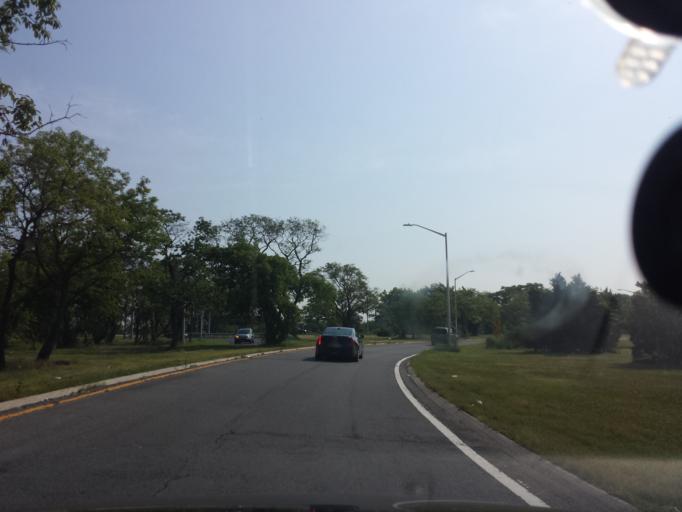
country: US
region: New York
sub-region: Kings County
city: Brooklyn
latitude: 40.5943
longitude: -73.9076
